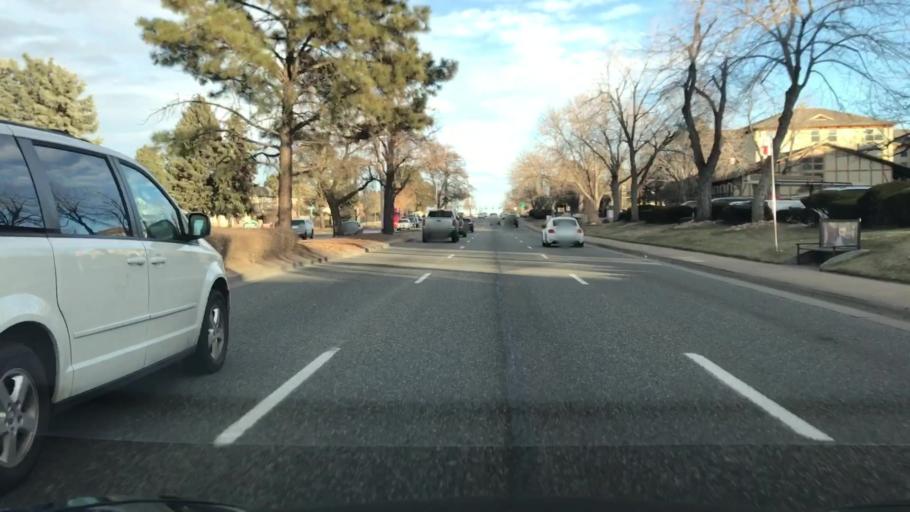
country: US
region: Colorado
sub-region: Adams County
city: Aurora
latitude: 39.6750
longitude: -104.8375
